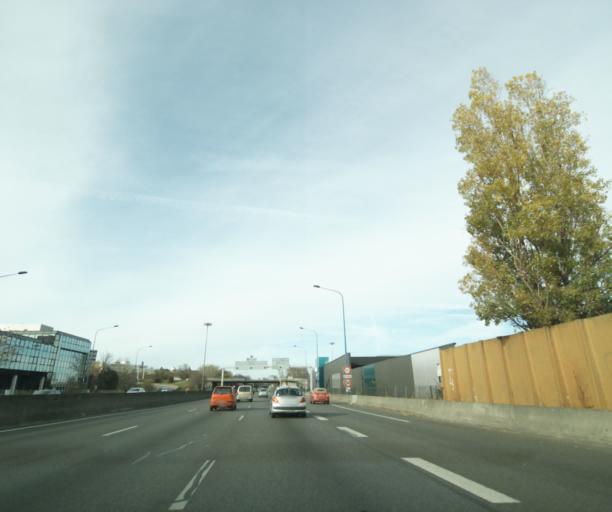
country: FR
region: Midi-Pyrenees
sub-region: Departement de la Haute-Garonne
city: Toulouse
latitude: 43.5835
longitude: 1.4038
